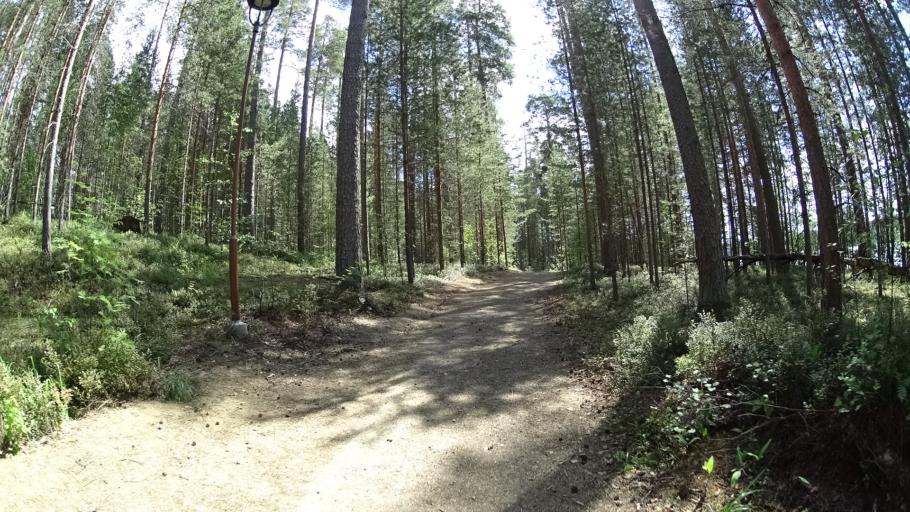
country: FI
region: Southern Savonia
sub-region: Savonlinna
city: Punkaharju
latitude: 61.7921
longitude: 29.3043
